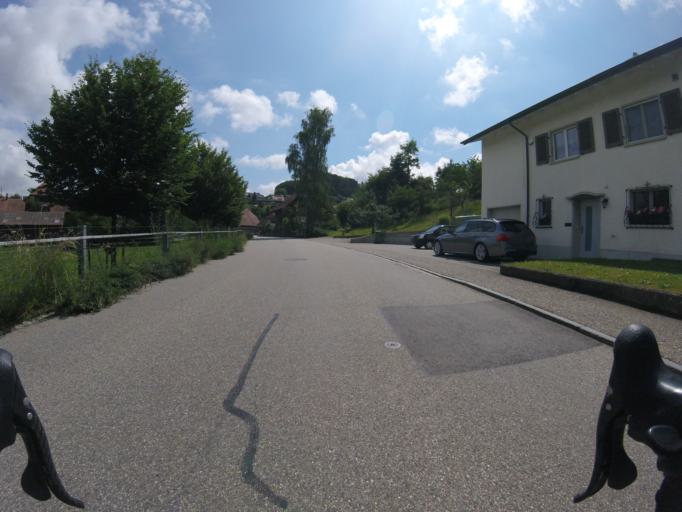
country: CH
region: Bern
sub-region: Bern-Mittelland District
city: Bariswil
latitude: 47.0196
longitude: 7.5248
